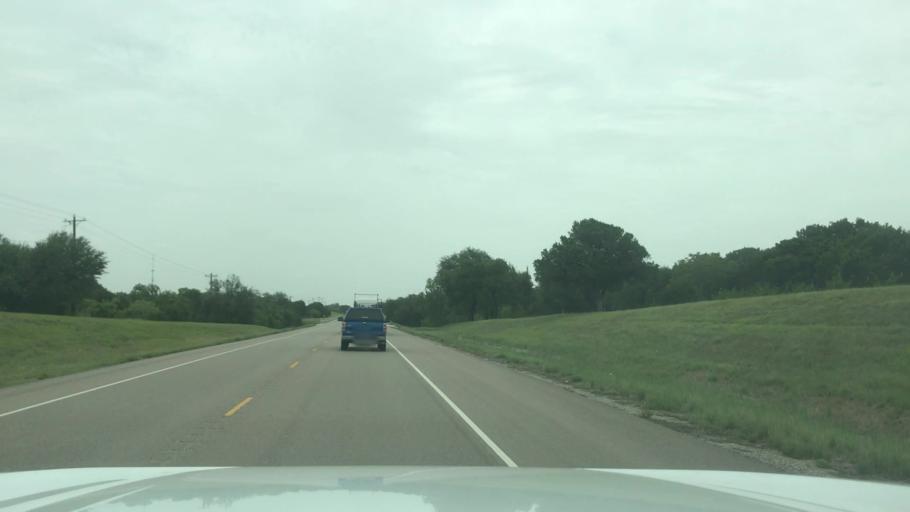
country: US
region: Texas
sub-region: Bosque County
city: Meridian
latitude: 31.9254
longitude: -97.6834
